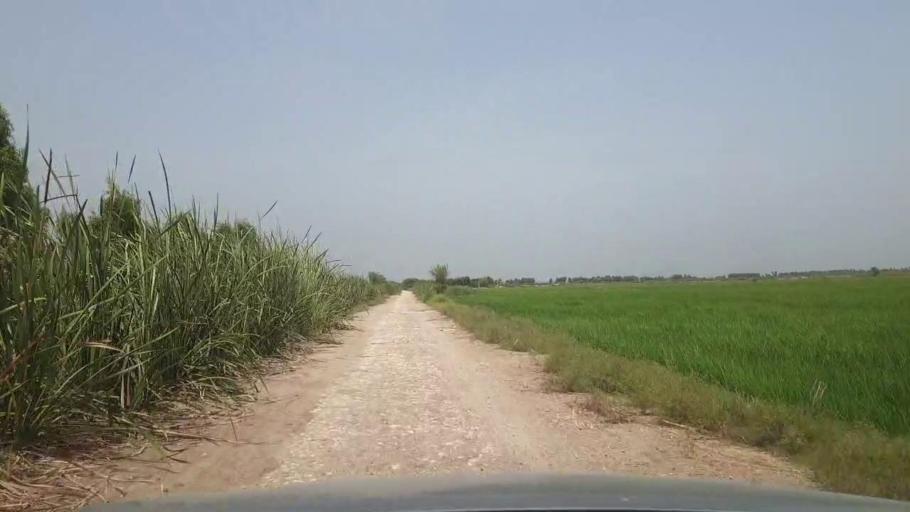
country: PK
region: Sindh
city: Garhi Yasin
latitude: 27.9414
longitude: 68.4304
